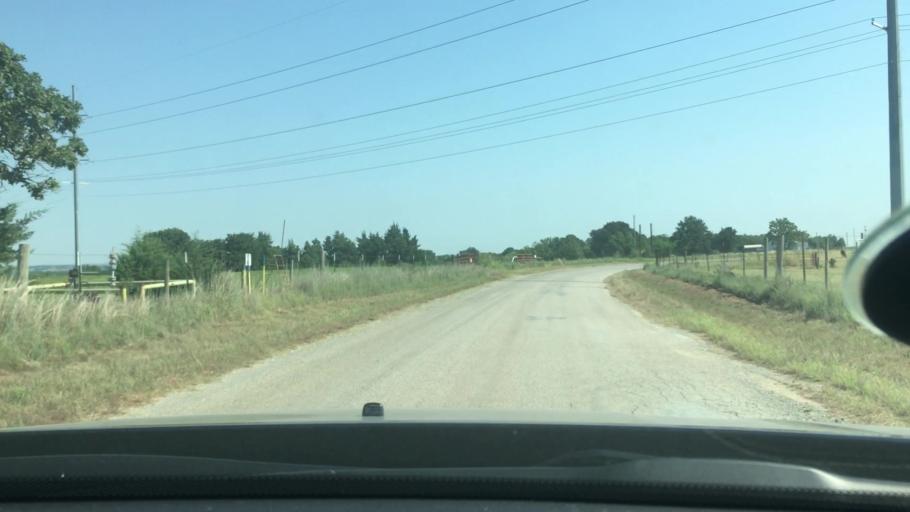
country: US
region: Oklahoma
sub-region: Garvin County
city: Lindsay
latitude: 34.7740
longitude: -97.6119
